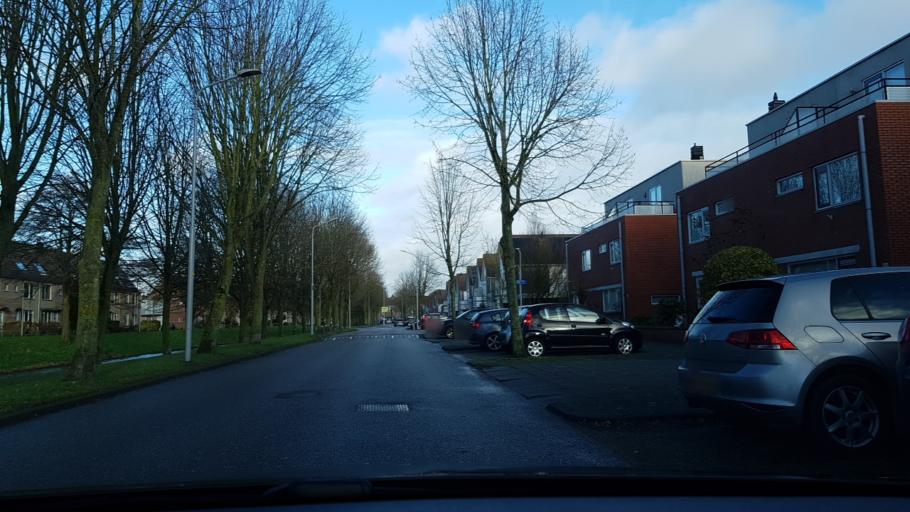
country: NL
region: North Holland
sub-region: Gemeente Haarlemmermeer
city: Hoofddorp
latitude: 52.2941
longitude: 4.6722
